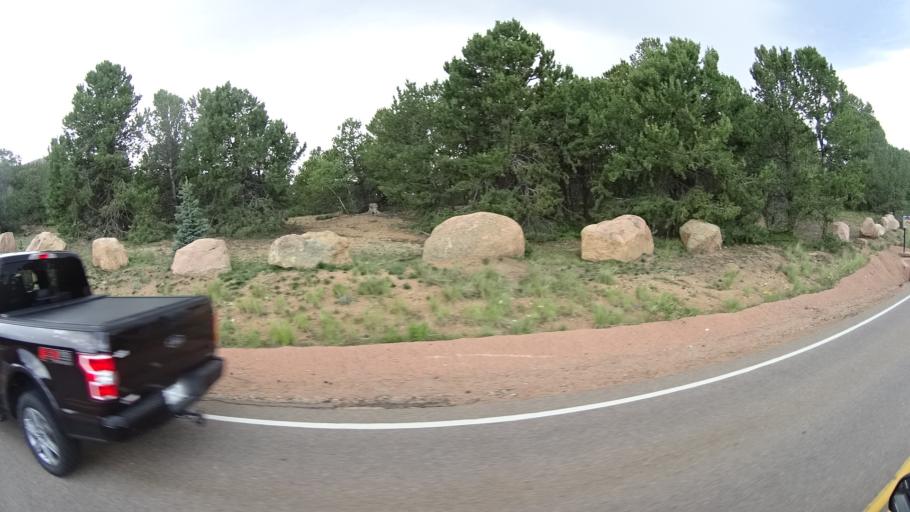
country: US
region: Colorado
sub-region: El Paso County
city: Cascade-Chipita Park
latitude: 38.8973
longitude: -105.0647
